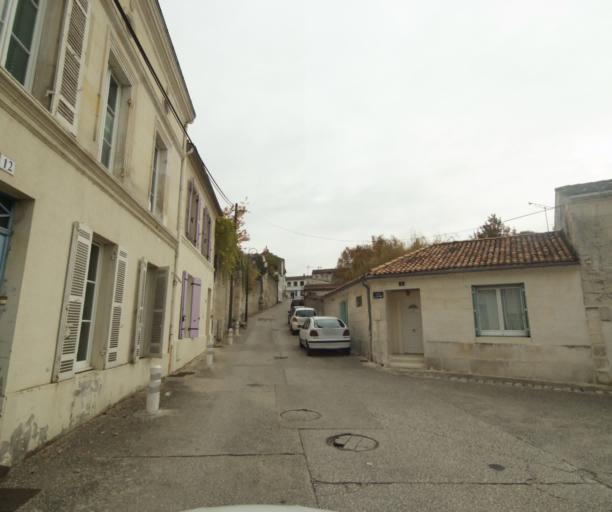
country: FR
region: Poitou-Charentes
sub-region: Departement de la Charente-Maritime
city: Saintes
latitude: 45.7424
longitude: -0.6418
